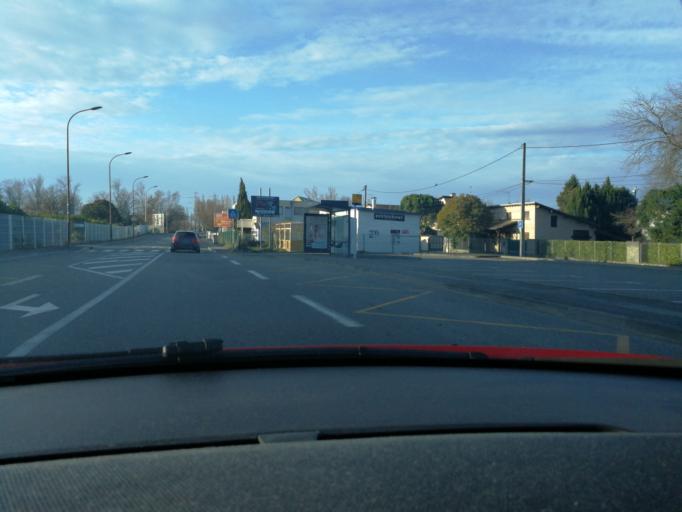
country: FR
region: Midi-Pyrenees
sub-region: Departement de la Haute-Garonne
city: Aucamville
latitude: 43.6454
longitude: 1.4196
